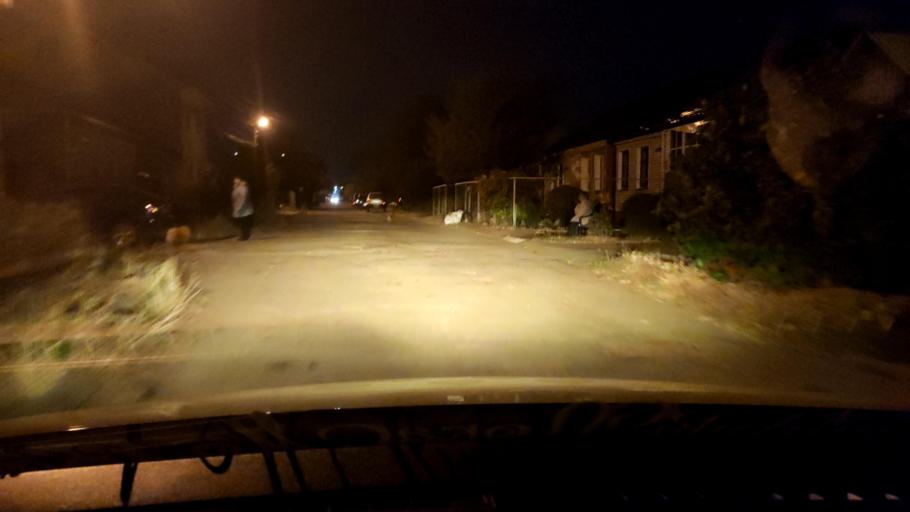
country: RU
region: Voronezj
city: Voronezh
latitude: 51.6981
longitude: 39.1593
